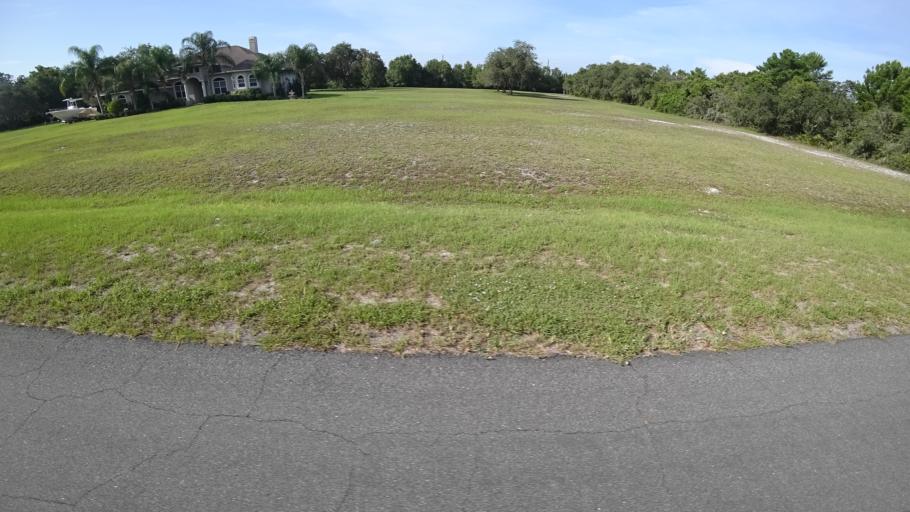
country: US
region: Florida
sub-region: Sarasota County
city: Lake Sarasota
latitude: 27.3518
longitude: -82.2491
